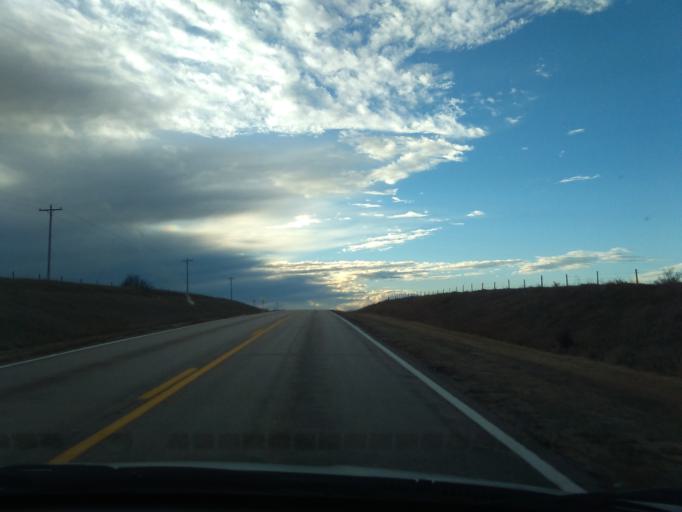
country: US
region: Nebraska
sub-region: Phelps County
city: Holdrege
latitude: 40.3072
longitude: -99.3517
